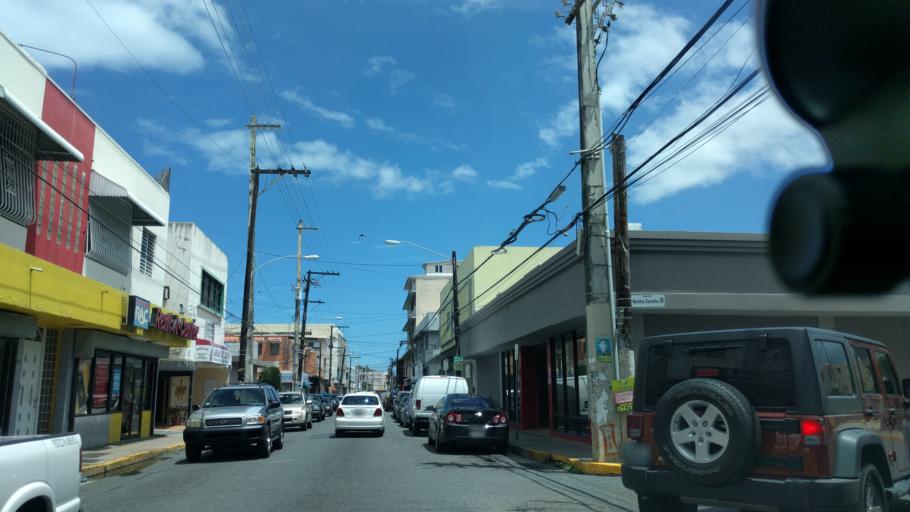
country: PR
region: San Juan
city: San Juan
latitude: 18.4512
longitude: -66.0570
